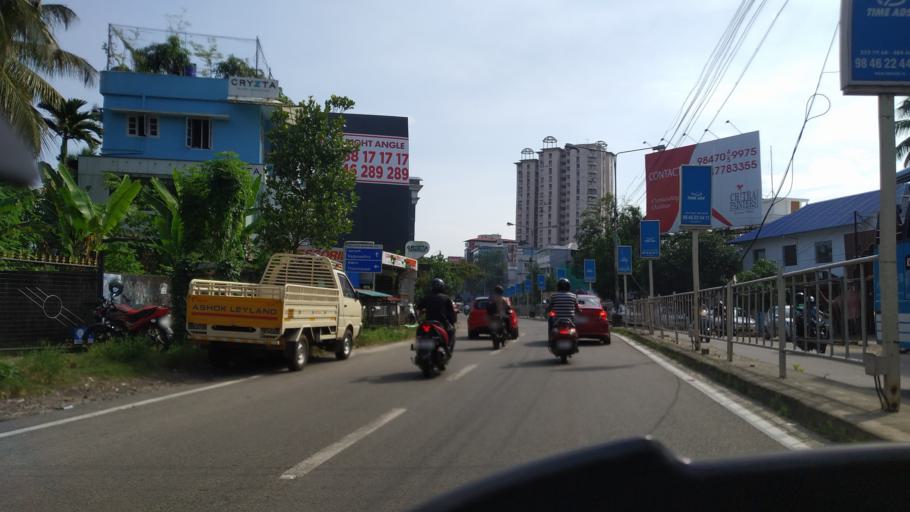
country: IN
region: Kerala
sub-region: Ernakulam
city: Cochin
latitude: 9.9852
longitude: 76.2959
